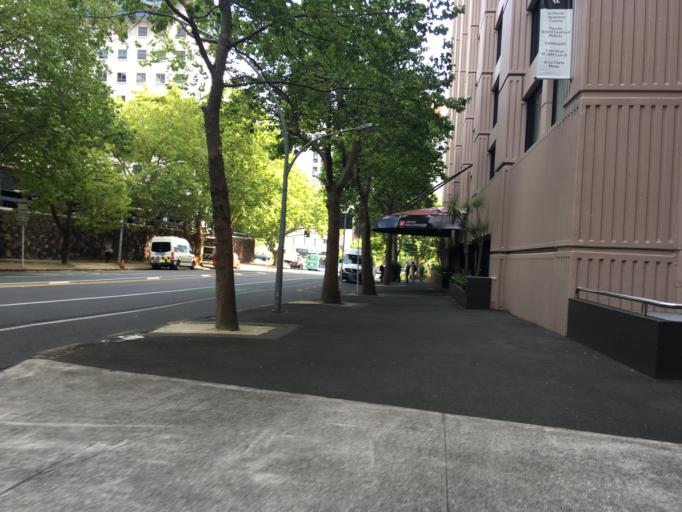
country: NZ
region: Auckland
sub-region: Auckland
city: Auckland
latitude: -36.8531
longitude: 174.7602
